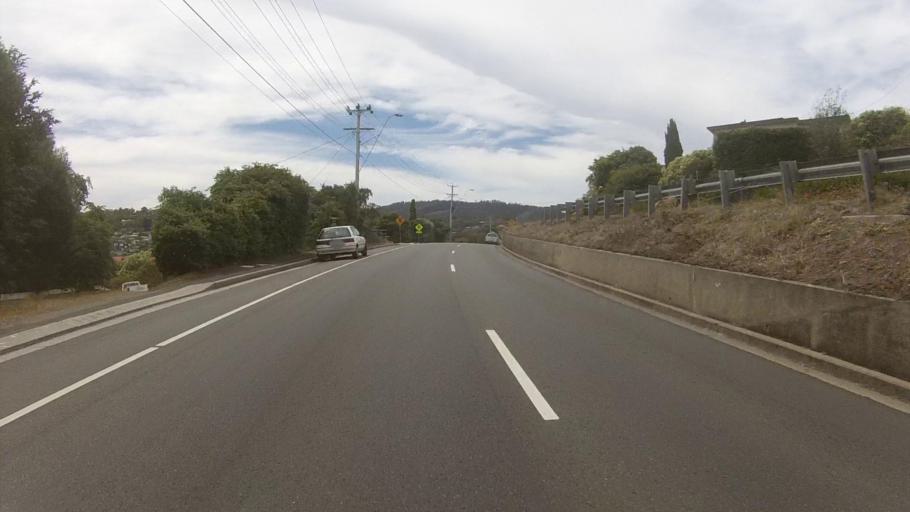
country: AU
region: Tasmania
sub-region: Clarence
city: Lindisfarne
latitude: -42.8533
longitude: 147.3577
